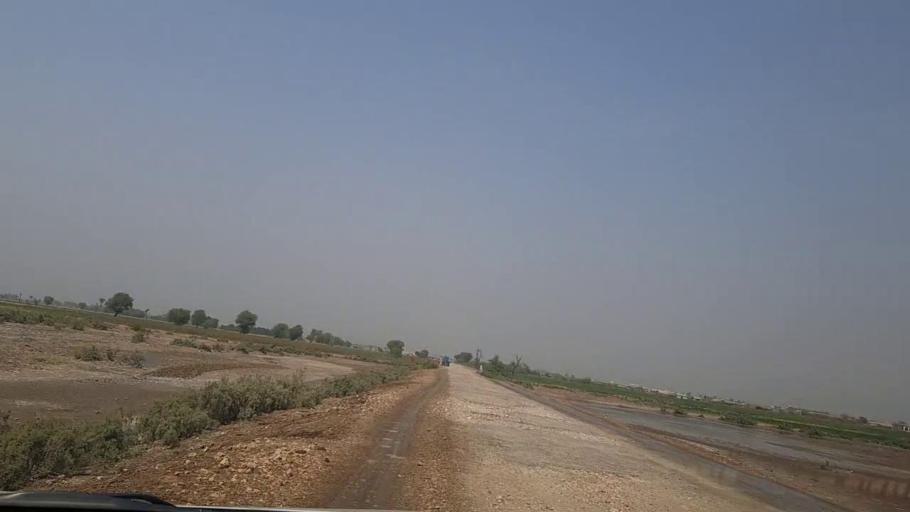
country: PK
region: Sindh
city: Pithoro
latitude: 25.5527
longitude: 69.2275
